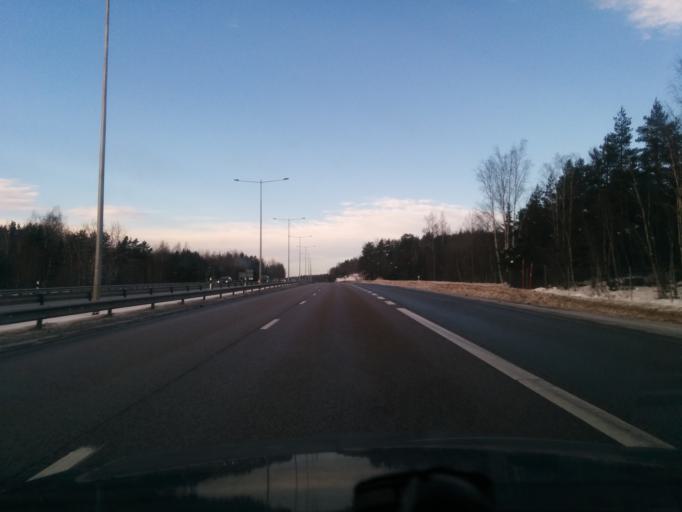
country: SE
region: Stockholm
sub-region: Upplands-Bro Kommun
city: Bro
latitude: 59.5341
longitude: 17.6267
